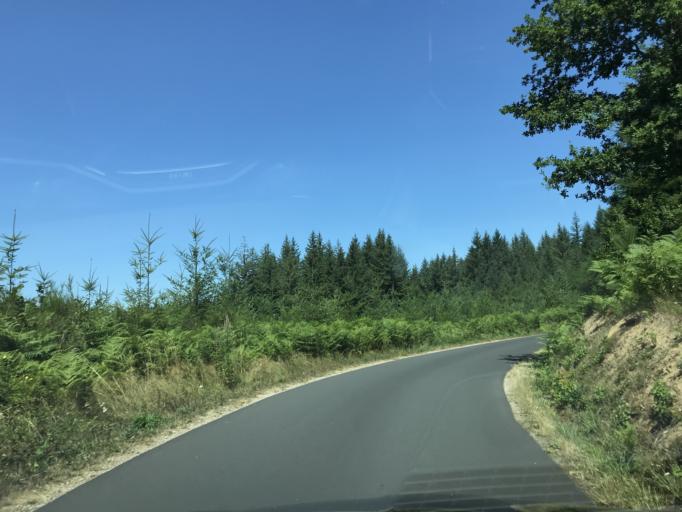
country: FR
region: Limousin
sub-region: Departement de la Correze
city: Neuvic
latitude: 45.3758
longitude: 2.2336
